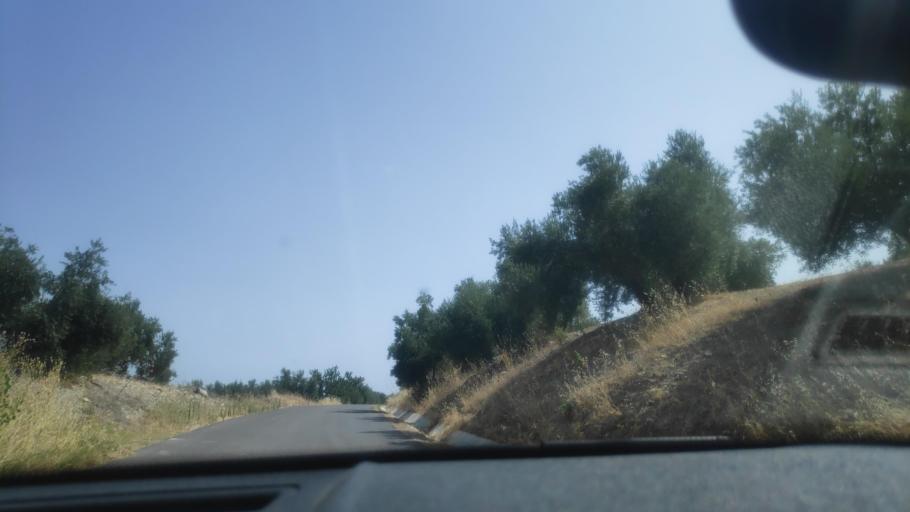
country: ES
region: Andalusia
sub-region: Provincia de Jaen
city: Jimena
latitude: 37.7912
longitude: -3.4525
